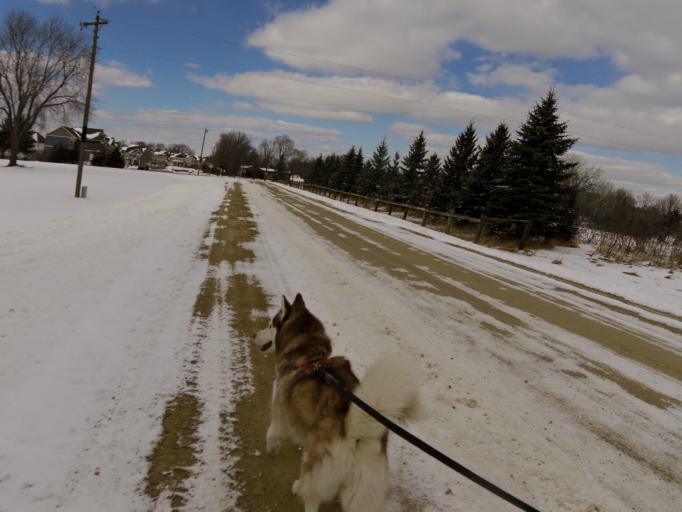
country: US
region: Minnesota
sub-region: Scott County
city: Prior Lake
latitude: 44.6874
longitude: -93.4527
